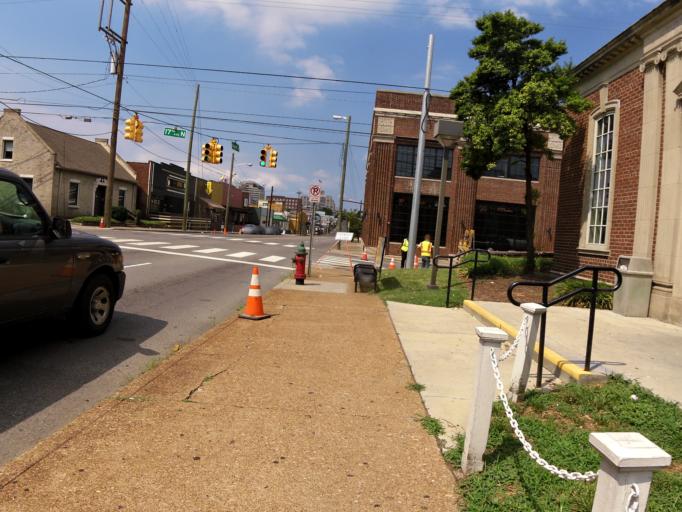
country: US
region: Tennessee
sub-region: Davidson County
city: Nashville
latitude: 36.1560
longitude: -86.7957
